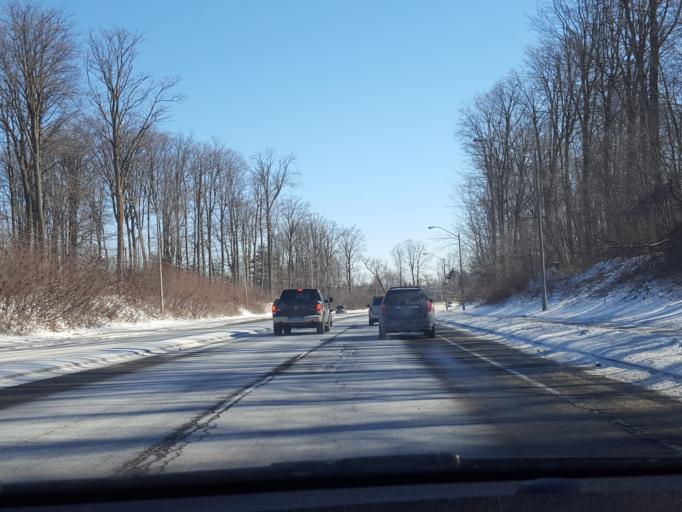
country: CA
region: Ontario
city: Kitchener
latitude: 43.4390
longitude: -80.5338
